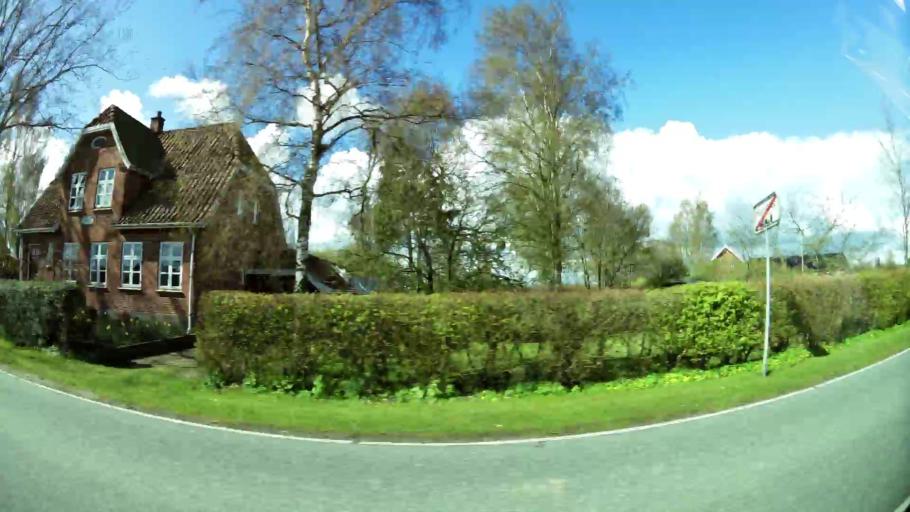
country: DK
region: South Denmark
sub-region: Middelfart Kommune
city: Brenderup
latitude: 55.4671
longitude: 10.0100
